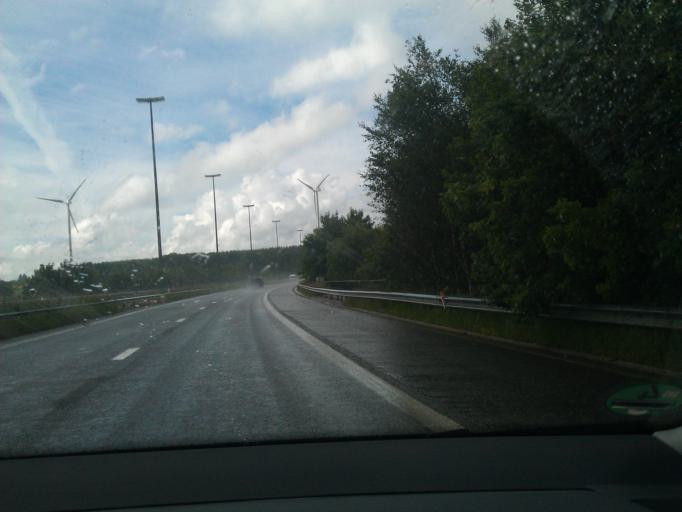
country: BE
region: Wallonia
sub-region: Province de Liege
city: Saint-Vith
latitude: 50.2963
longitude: 6.0841
